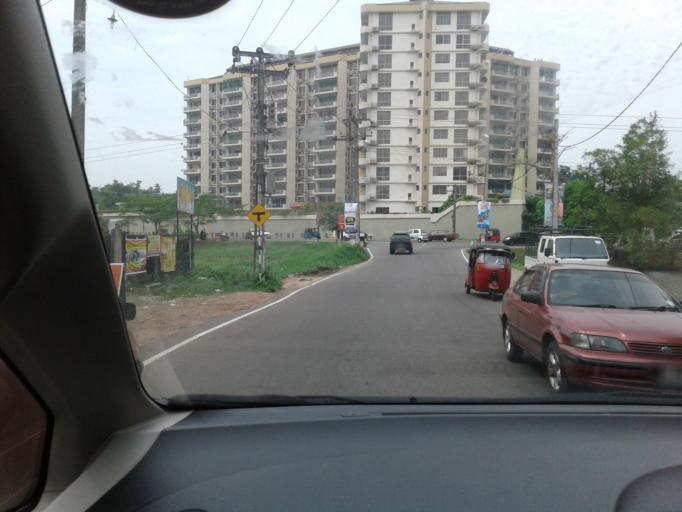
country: LK
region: Western
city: Maharagama
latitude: 6.8655
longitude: 79.9296
